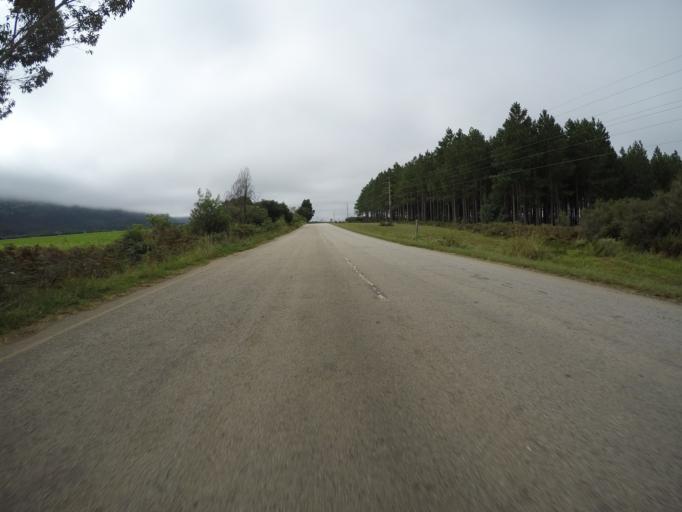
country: ZA
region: Eastern Cape
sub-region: Cacadu District Municipality
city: Kareedouw
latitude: -33.9961
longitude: 24.1346
